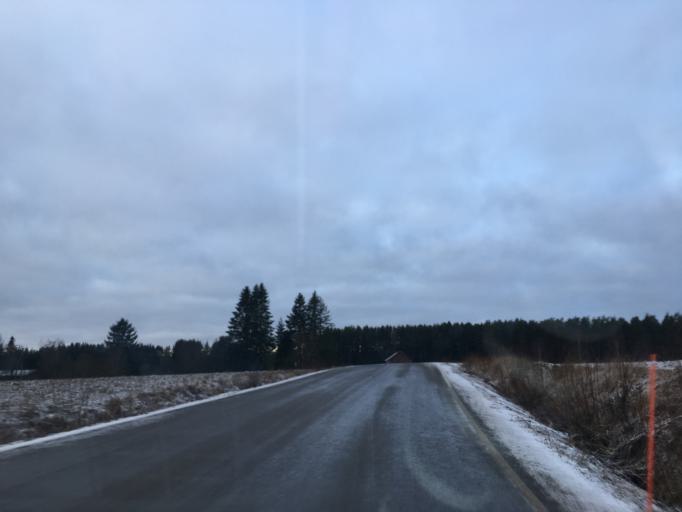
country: FI
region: Varsinais-Suomi
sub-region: Turku
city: Lieto
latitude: 60.5811
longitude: 22.5094
